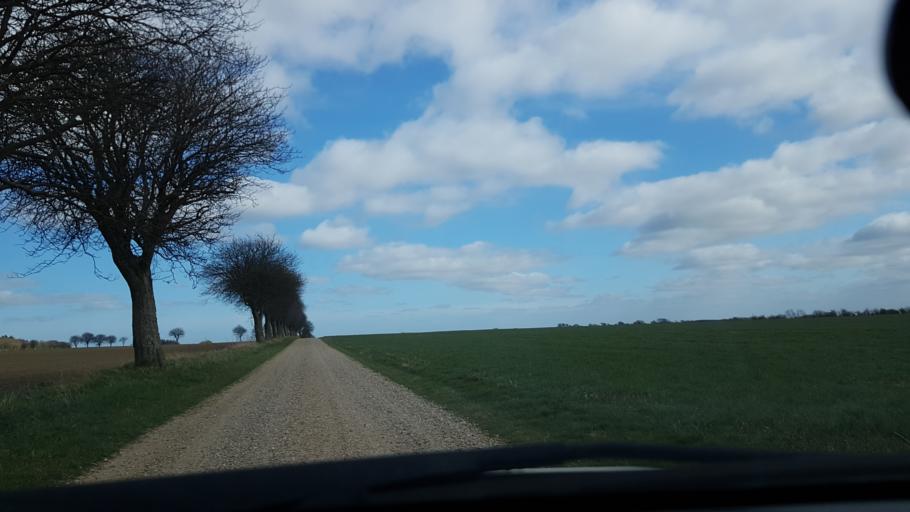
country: DK
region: South Denmark
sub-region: Vejen Kommune
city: Brorup
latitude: 55.4261
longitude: 9.0216
